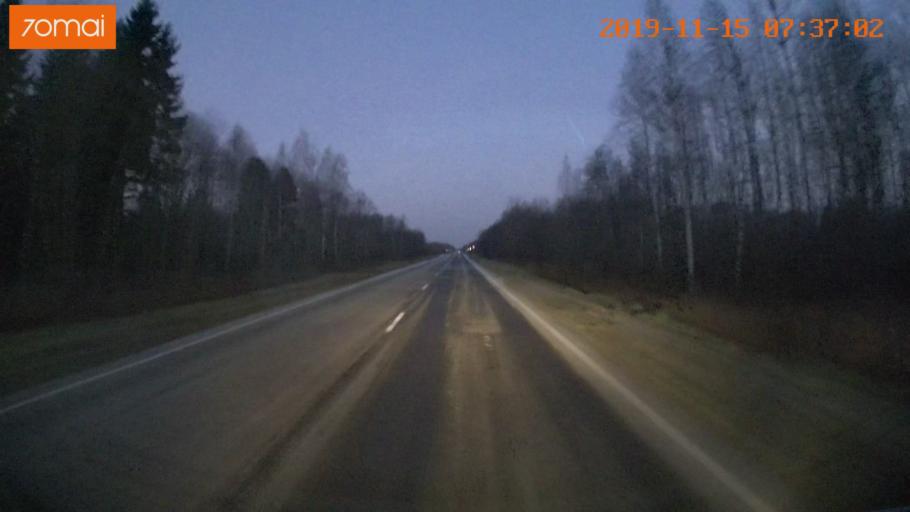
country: RU
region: Vologda
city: Sheksna
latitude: 58.7441
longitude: 38.4267
